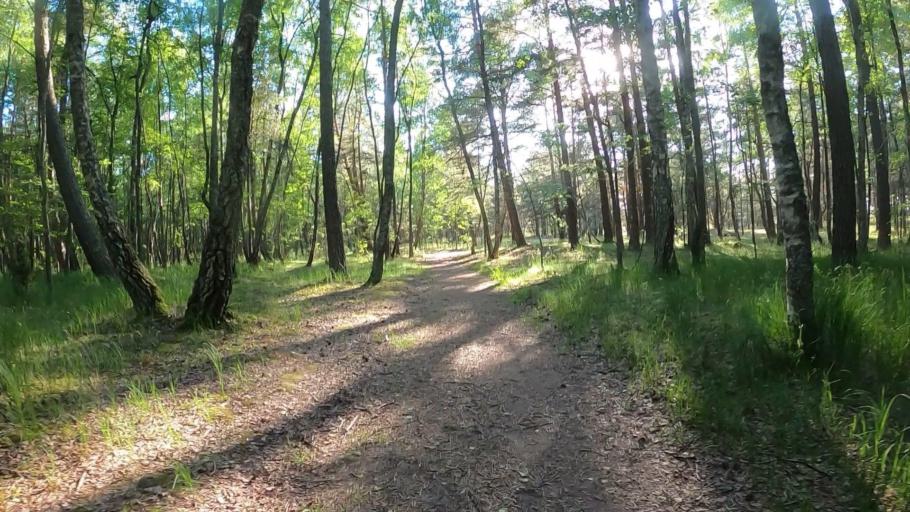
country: LV
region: Carnikava
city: Carnikava
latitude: 57.1386
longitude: 24.2399
